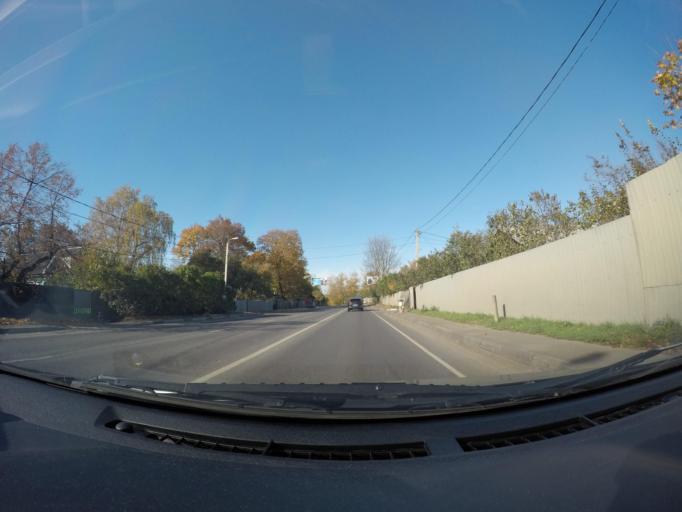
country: RU
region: Moskovskaya
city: Kraskovo
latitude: 55.6327
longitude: 37.9702
